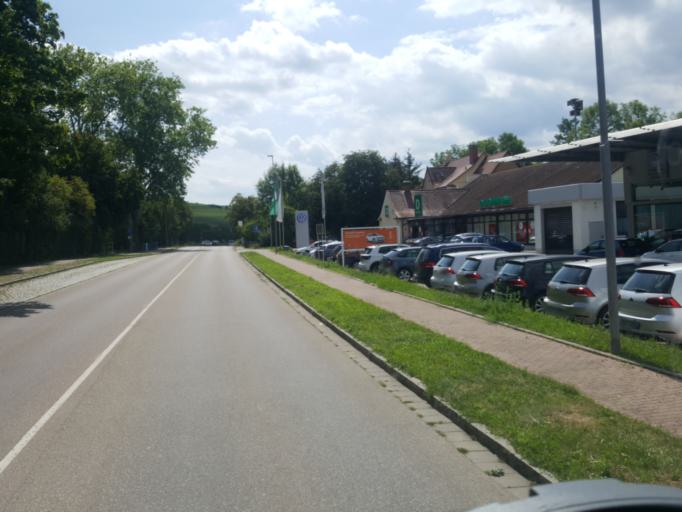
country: DE
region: Baden-Wuerttemberg
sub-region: Freiburg Region
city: Mullheim
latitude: 47.8109
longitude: 7.6095
